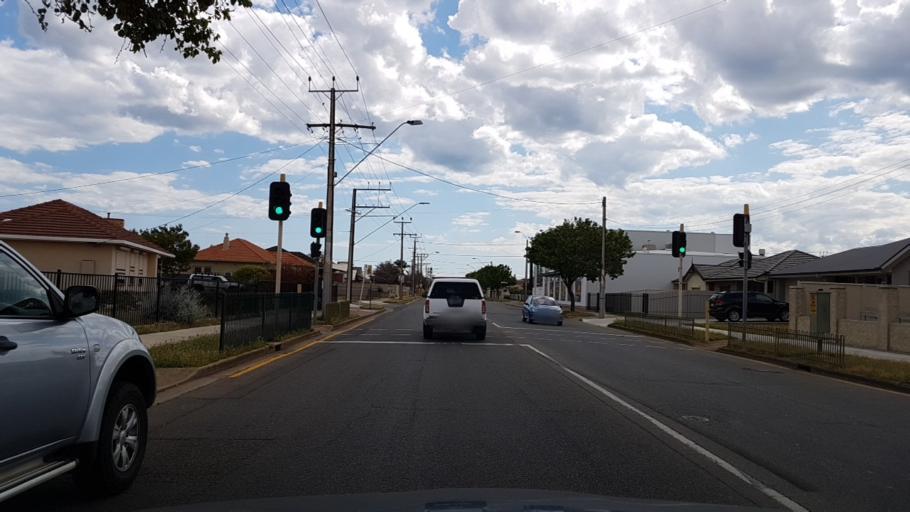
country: AU
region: South Australia
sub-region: Charles Sturt
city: Seaton
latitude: -34.8911
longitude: 138.5211
